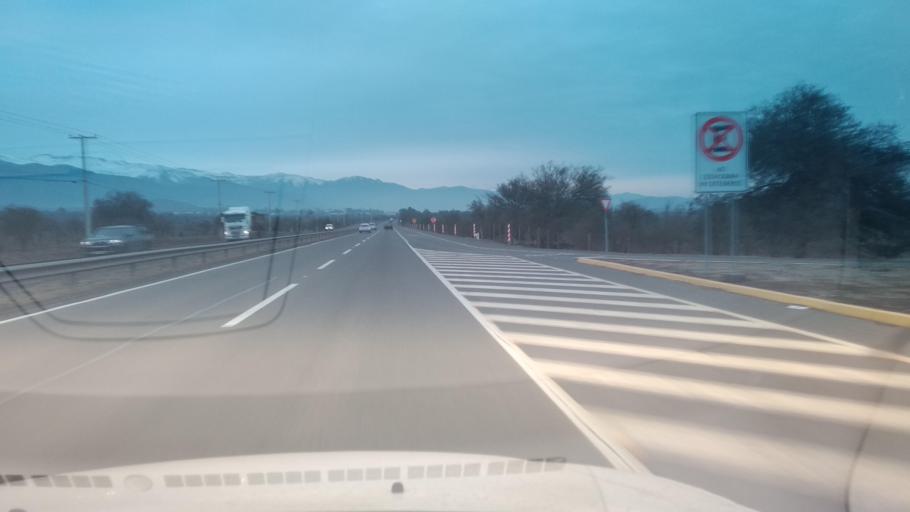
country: CL
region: Santiago Metropolitan
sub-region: Provincia de Chacabuco
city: Chicureo Abajo
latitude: -33.1233
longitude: -70.6766
